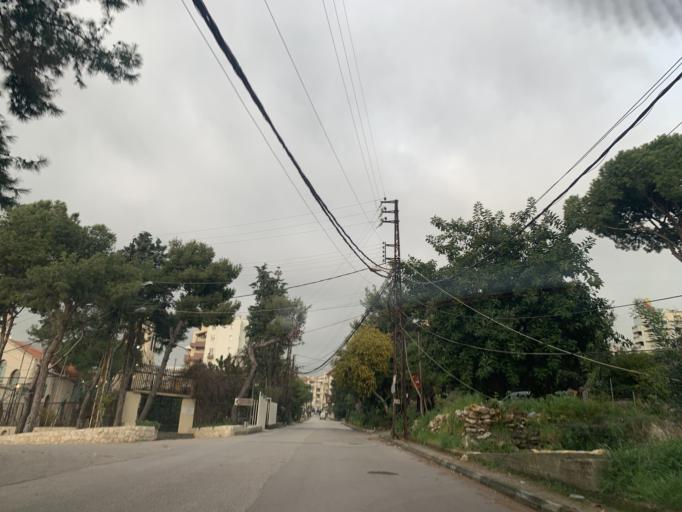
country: LB
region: Mont-Liban
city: Djounie
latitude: 34.0073
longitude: 35.6464
